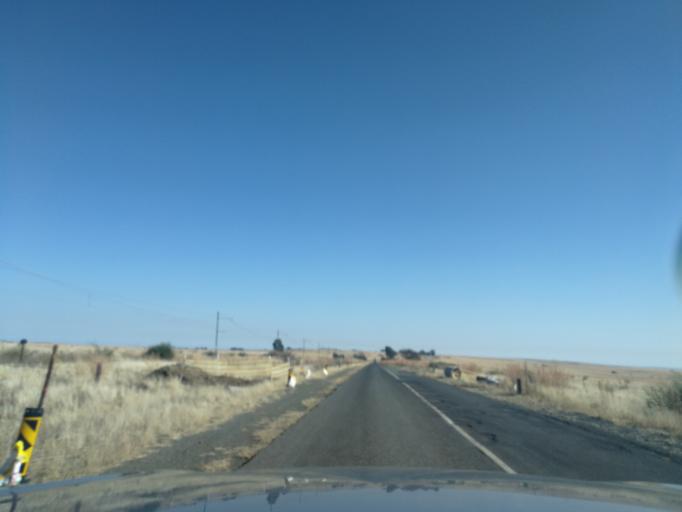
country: ZA
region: Orange Free State
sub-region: Fezile Dabi District Municipality
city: Kroonstad
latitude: -27.8925
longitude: 27.4870
